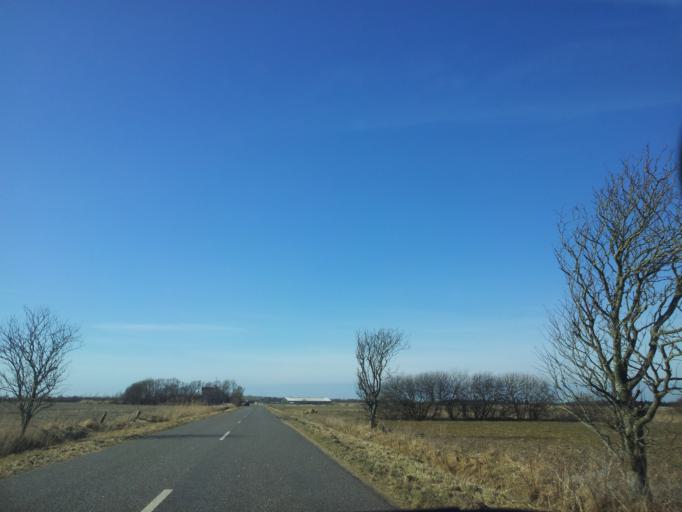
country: DK
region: South Denmark
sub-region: Tonder Kommune
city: Sherrebek
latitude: 55.1702
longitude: 8.7369
